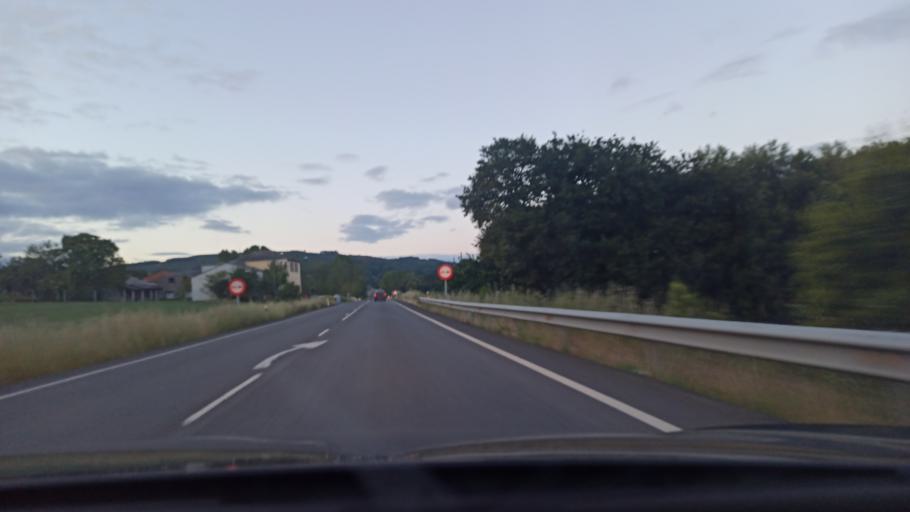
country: ES
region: Galicia
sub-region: Provincia de Lugo
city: Guntin
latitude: 42.9117
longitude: -7.6672
